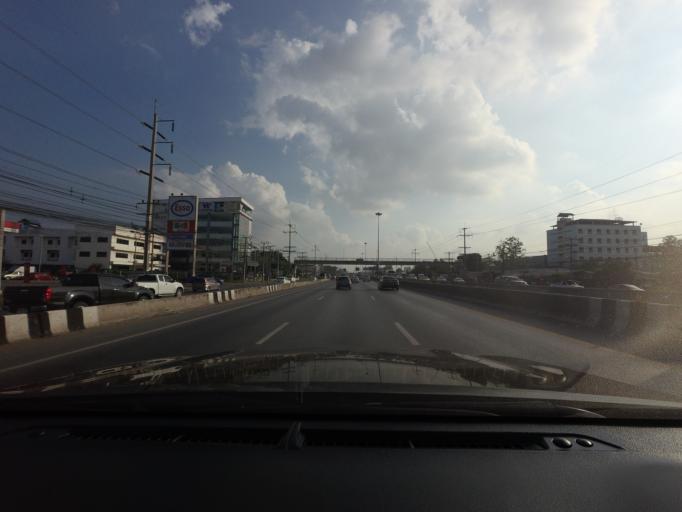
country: TH
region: Pathum Thani
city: Khlong Luang
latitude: 14.0571
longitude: 100.6171
